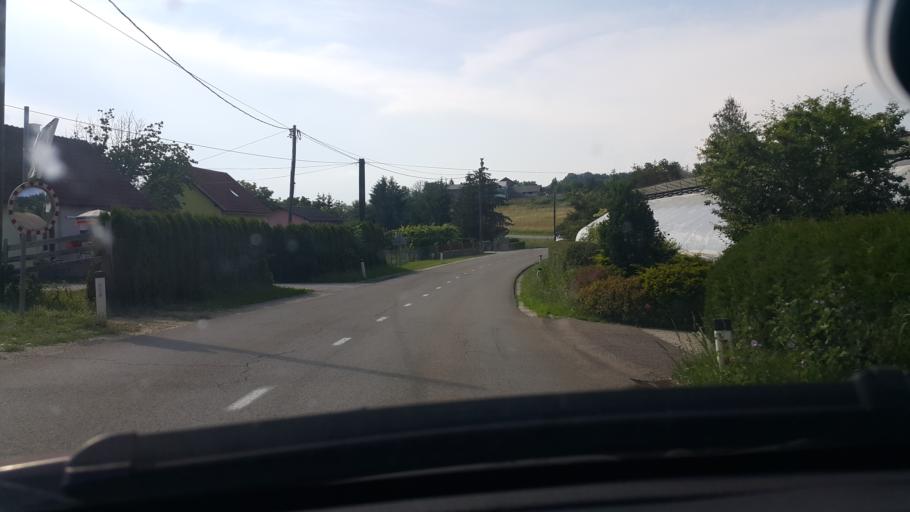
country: SI
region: Duplek
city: Spodnji Duplek
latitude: 46.4986
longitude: 15.7610
